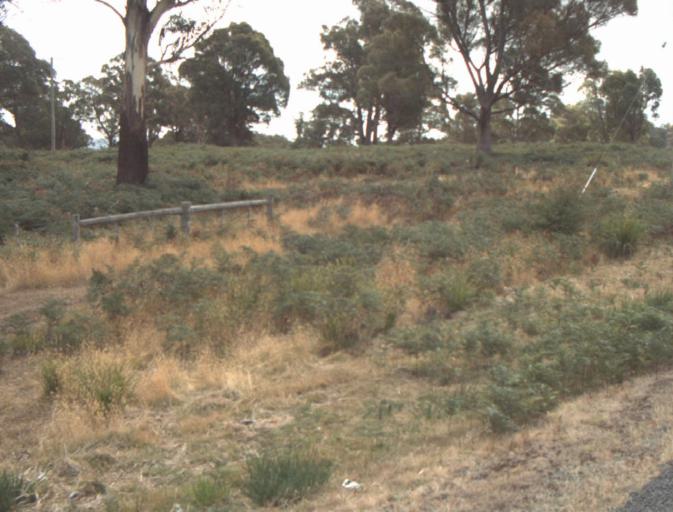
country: AU
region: Tasmania
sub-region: Launceston
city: Mayfield
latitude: -41.2794
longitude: 147.0380
